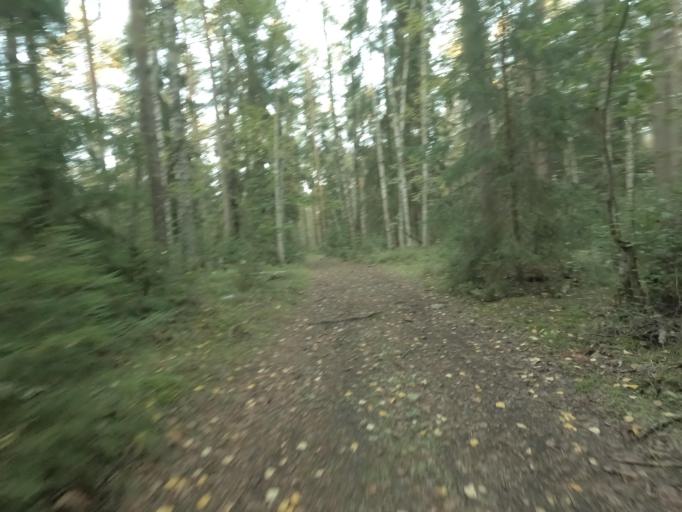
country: RU
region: Leningrad
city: Otradnoye
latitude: 59.8266
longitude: 30.8206
